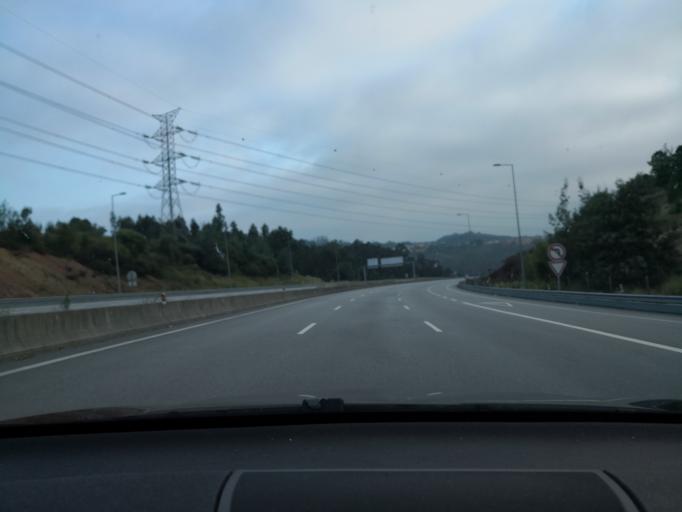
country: PT
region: Porto
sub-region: Gondomar
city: Foz do Sousa
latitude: 41.0663
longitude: -8.4526
